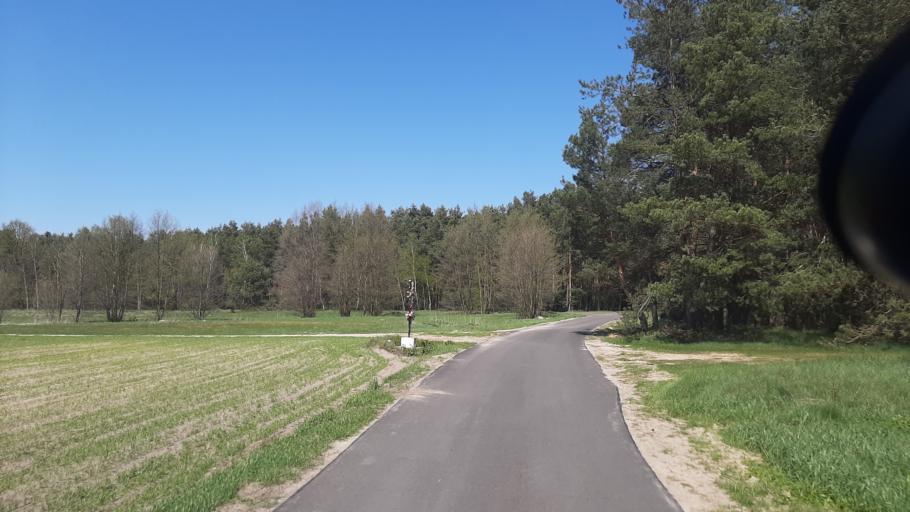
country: PL
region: Lublin Voivodeship
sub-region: Powiat lubartowski
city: Abramow
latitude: 51.4071
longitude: 22.3229
